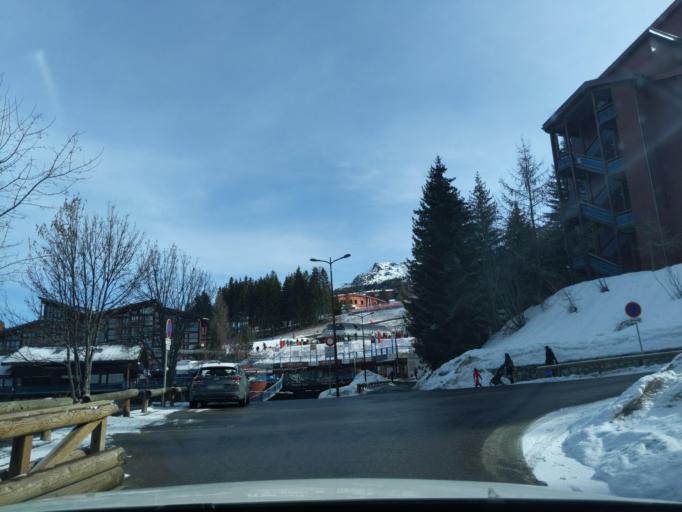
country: FR
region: Rhone-Alpes
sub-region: Departement de la Savoie
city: Bourg-Saint-Maurice
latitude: 45.5712
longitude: 6.7775
